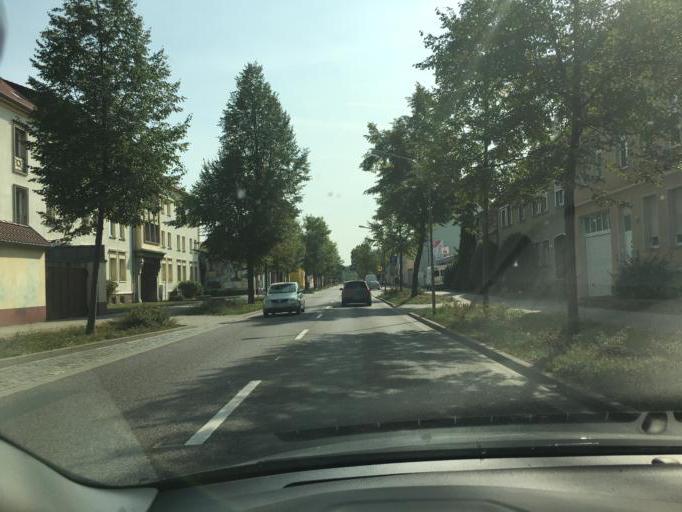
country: DE
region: Saxony-Anhalt
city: Calbe
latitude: 51.9105
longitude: 11.7753
